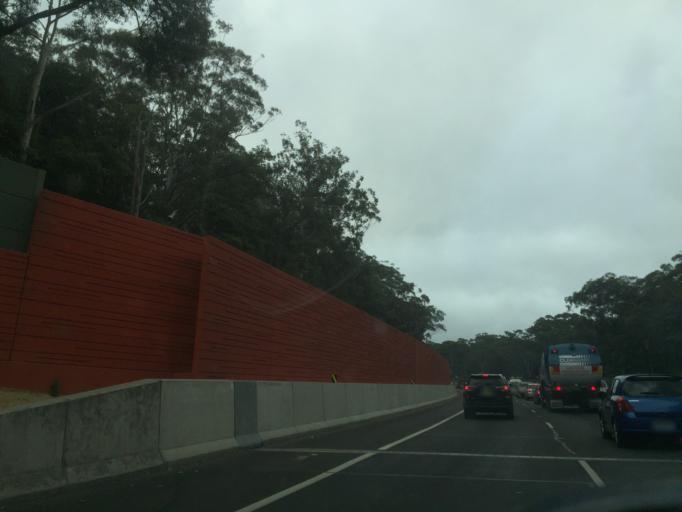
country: AU
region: New South Wales
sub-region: Hornsby Shire
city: Beecroft
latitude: -33.7572
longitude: 151.0615
